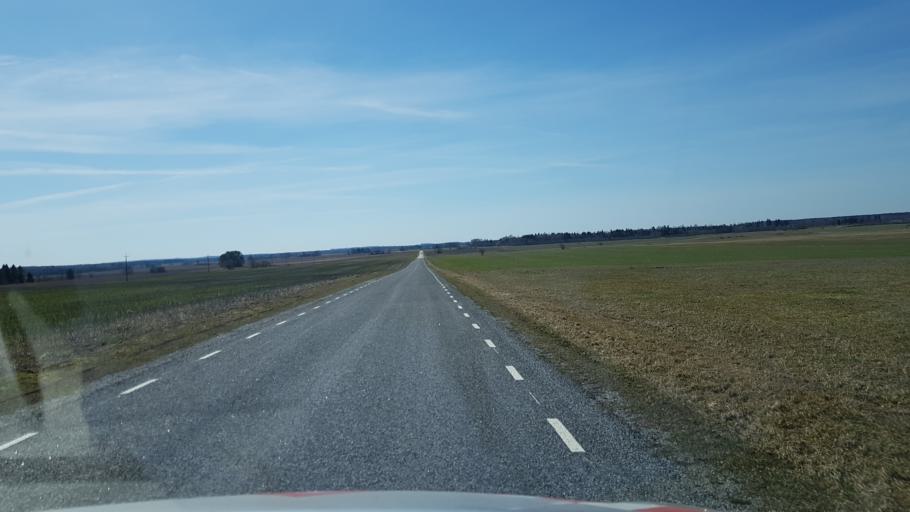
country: EE
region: Laeaene-Virumaa
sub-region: Vinni vald
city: Vinni
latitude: 59.0895
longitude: 26.4700
